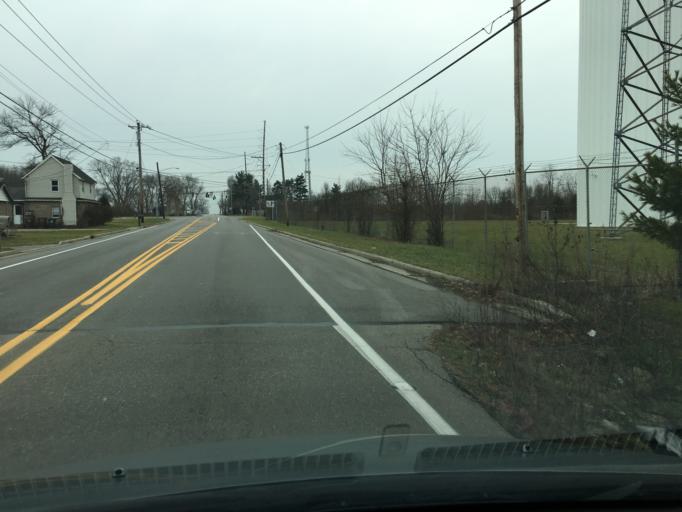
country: US
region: Ohio
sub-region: Hamilton County
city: Highpoint
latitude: 39.3210
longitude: -84.3314
